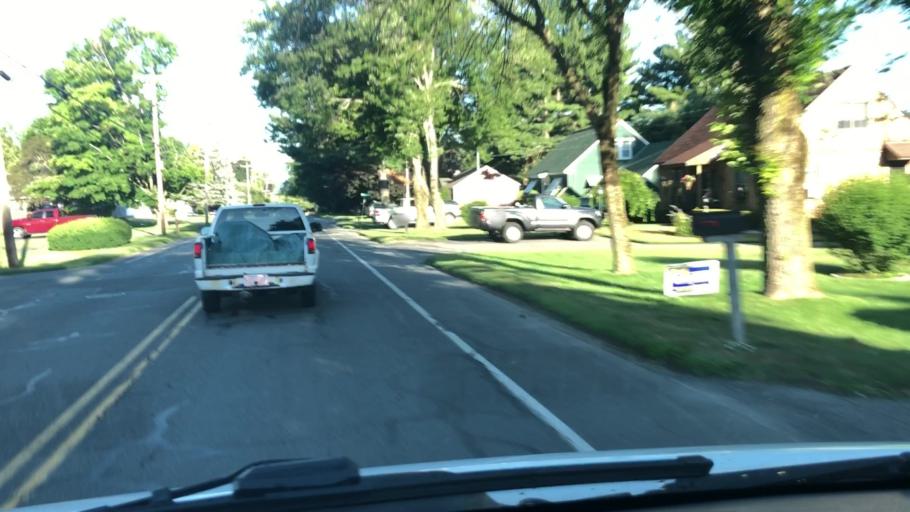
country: US
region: Massachusetts
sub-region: Berkshire County
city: Dalton
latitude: 42.4524
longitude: -73.1945
